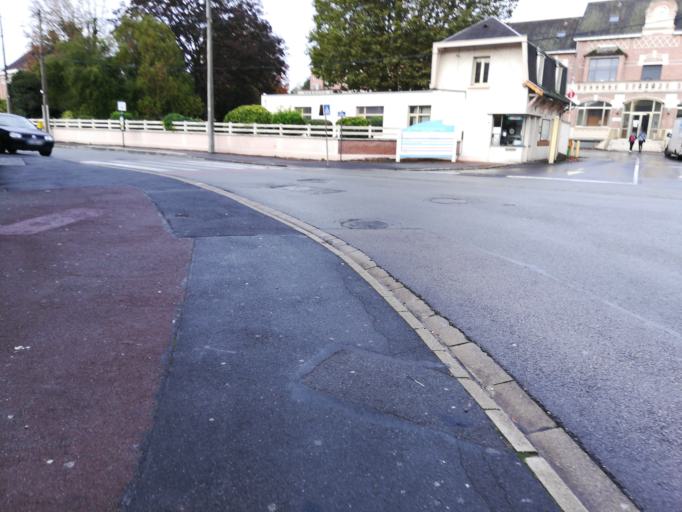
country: FR
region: Nord-Pas-de-Calais
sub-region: Departement du Pas-de-Calais
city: Montigny-en-Gohelle
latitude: 50.4302
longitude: 2.9465
